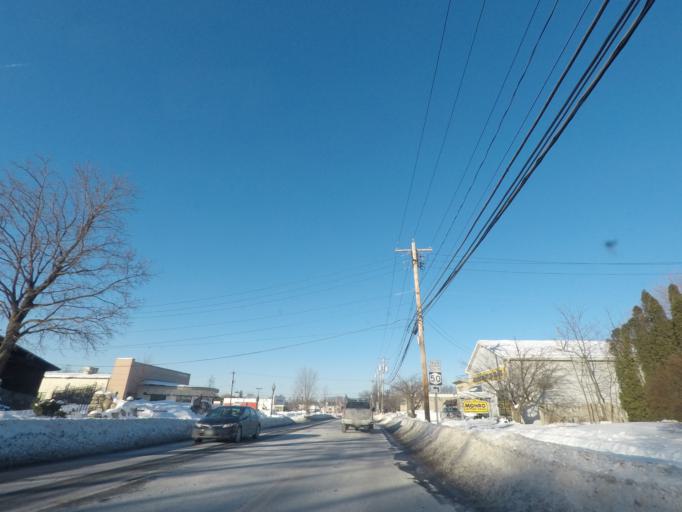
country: US
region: New York
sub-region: Saratoga County
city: Saratoga Springs
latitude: 43.0694
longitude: -73.7888
